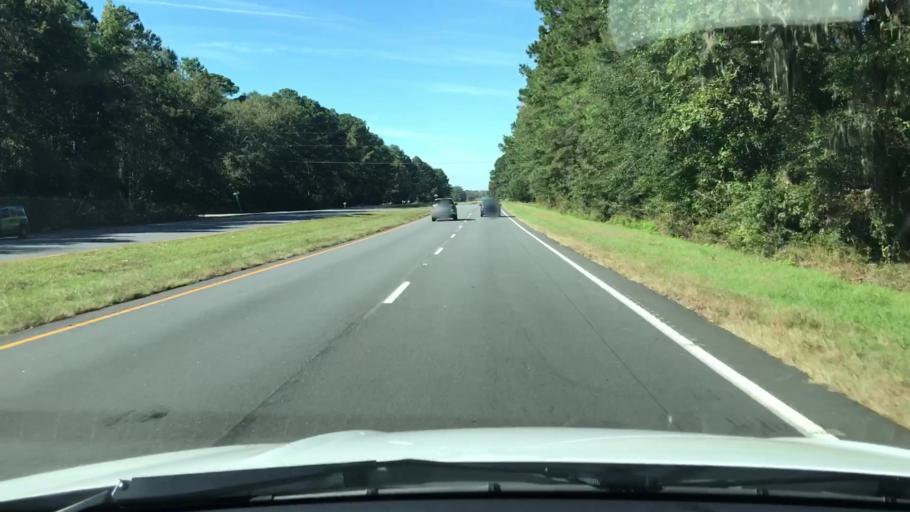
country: US
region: South Carolina
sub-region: Hampton County
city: Yemassee
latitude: 32.5908
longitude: -80.7485
